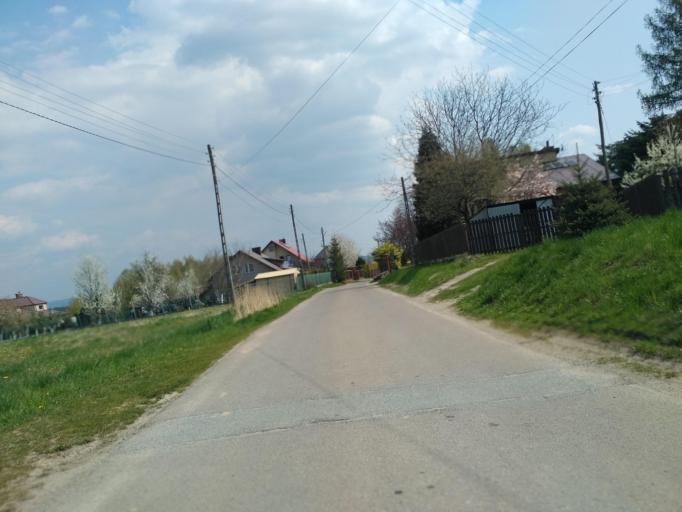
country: PL
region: Subcarpathian Voivodeship
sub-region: Powiat jasielski
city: Jaslo
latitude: 49.7179
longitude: 21.5046
